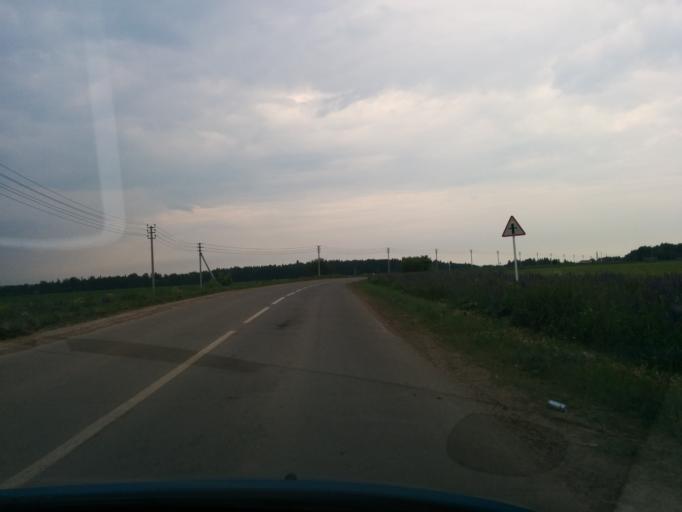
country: RU
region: Perm
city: Polazna
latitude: 58.2374
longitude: 56.2798
